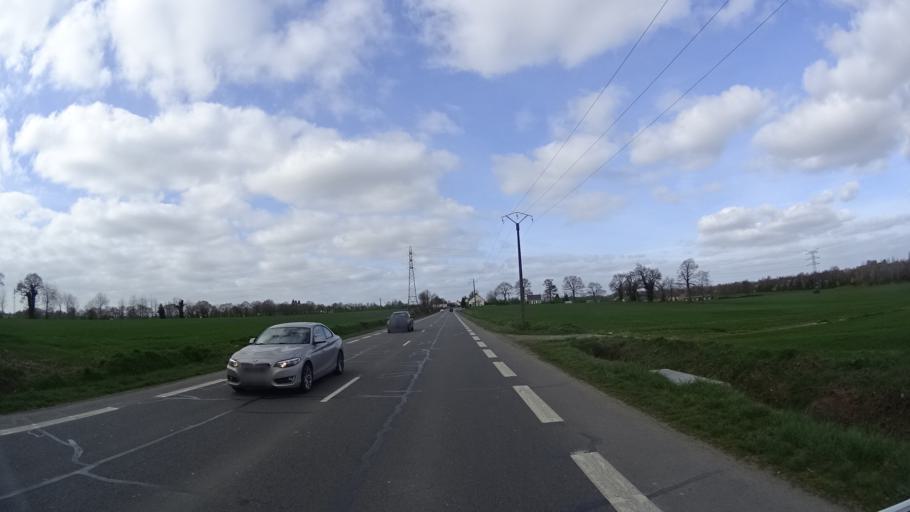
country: FR
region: Brittany
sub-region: Departement d'Ille-et-Vilaine
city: Montgermont
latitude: 48.1653
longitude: -1.7150
